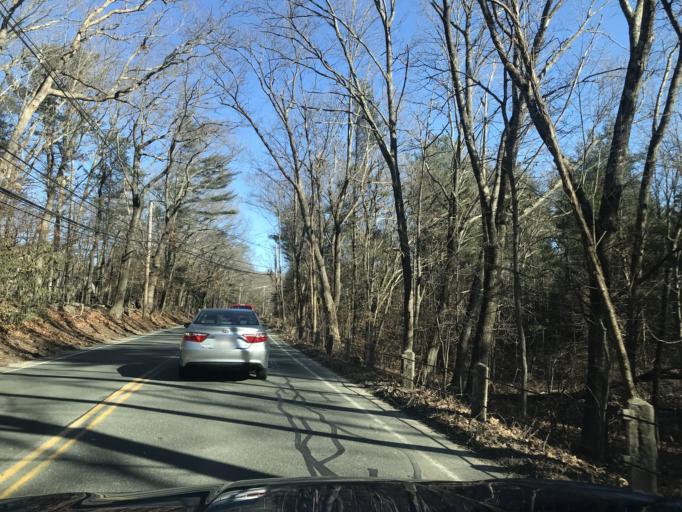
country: US
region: Massachusetts
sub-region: Essex County
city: Groveland
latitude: 42.7110
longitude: -71.0563
